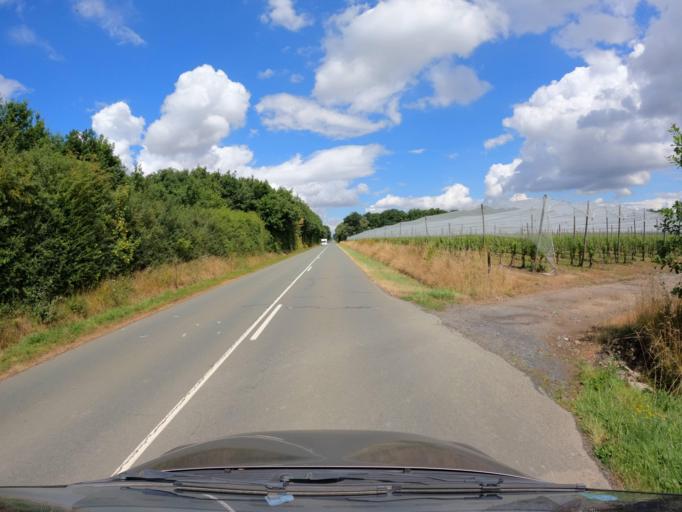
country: FR
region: Pays de la Loire
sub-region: Departement de Maine-et-Loire
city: Champigne
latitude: 47.6848
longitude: -0.5557
